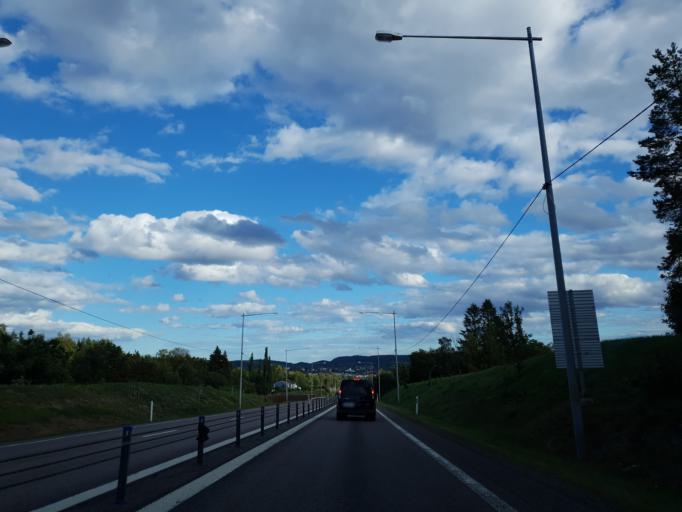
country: SE
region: Vaesternorrland
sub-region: Haernoesands Kommun
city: Haernoesand
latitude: 62.6471
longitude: 17.9003
